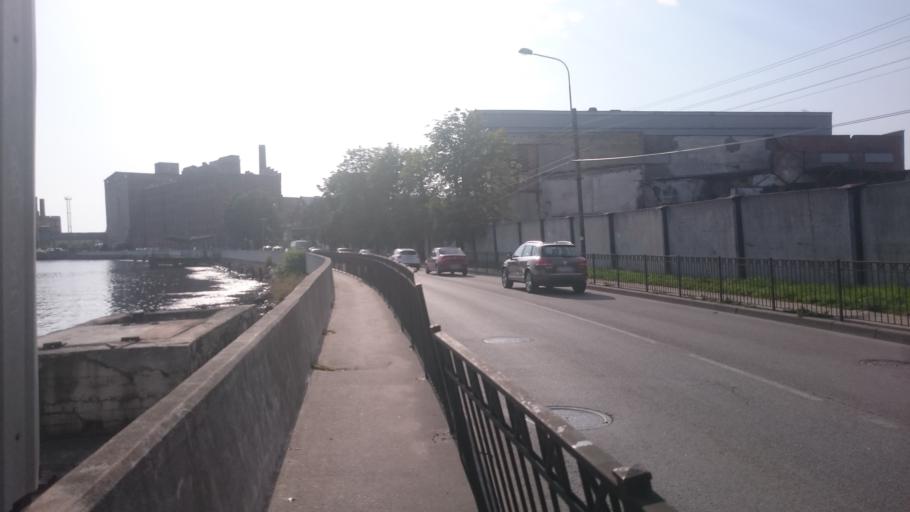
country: RU
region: Kaliningrad
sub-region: Gorod Kaliningrad
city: Kaliningrad
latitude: 54.7080
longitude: 20.4612
